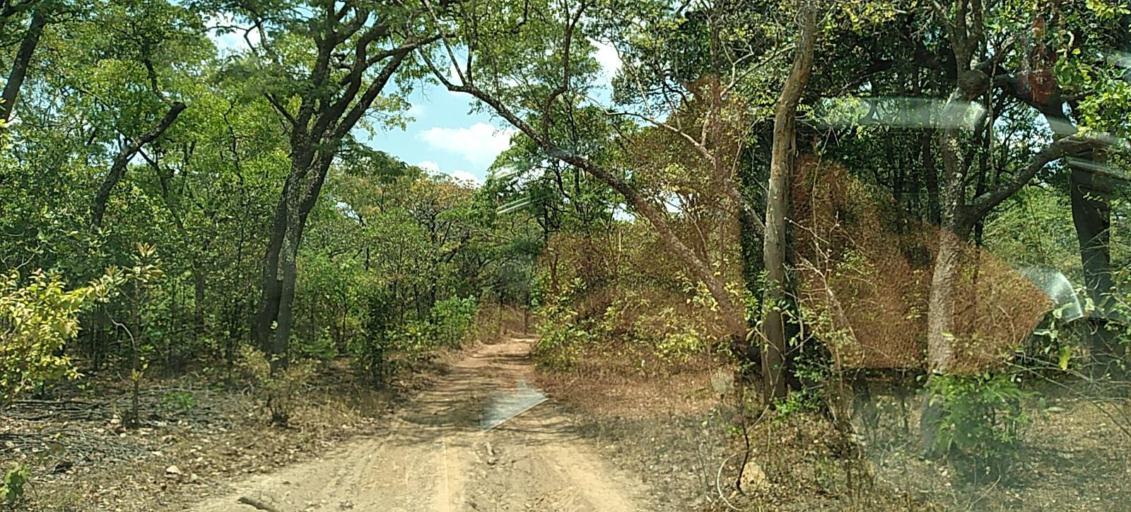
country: ZM
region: Copperbelt
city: Chililabombwe
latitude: -12.4673
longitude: 27.6996
